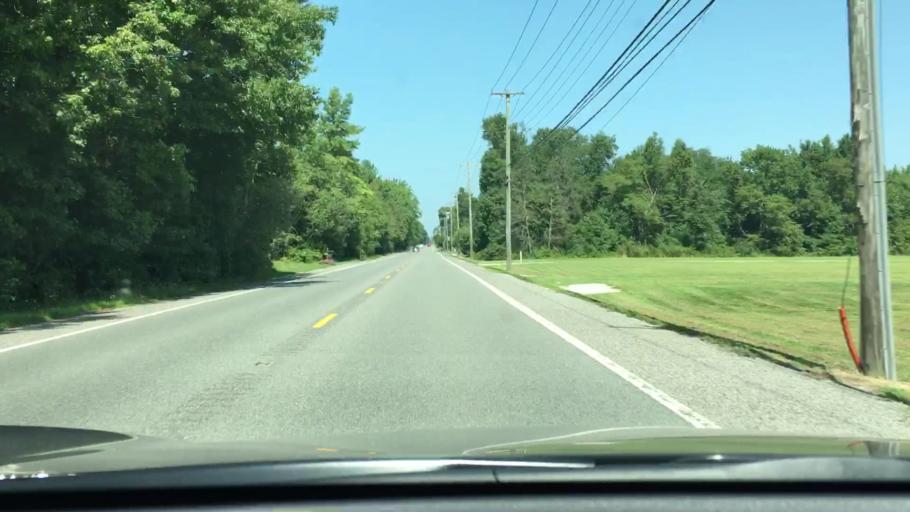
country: US
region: New Jersey
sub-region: Cumberland County
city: Laurel Lake
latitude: 39.3003
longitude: -75.0016
